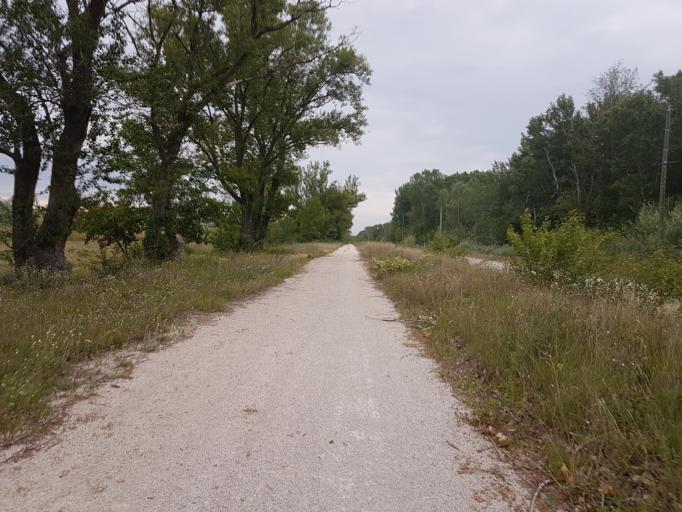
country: FR
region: Languedoc-Roussillon
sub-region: Departement du Gard
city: Montfaucon
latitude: 44.0679
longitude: 4.7731
